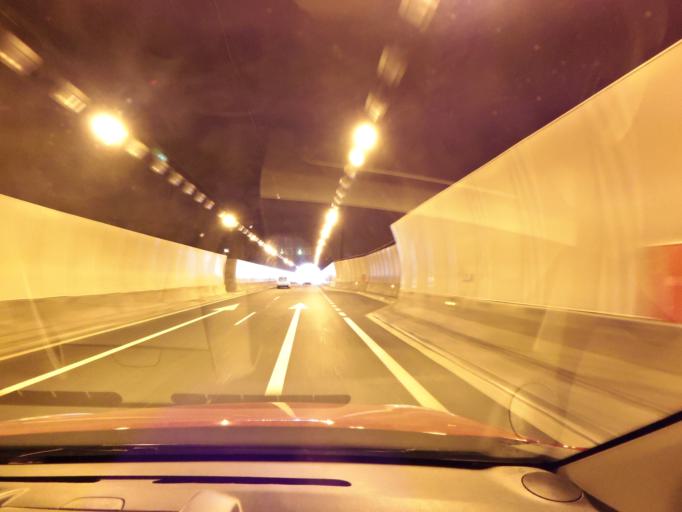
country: ES
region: Canary Islands
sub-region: Provincia de Las Palmas
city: Puerto Rico
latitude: 27.7992
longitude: -15.7044
